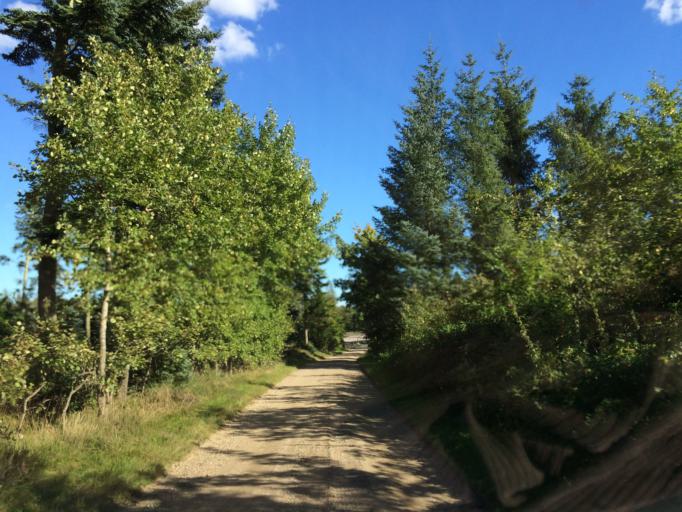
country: DK
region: Central Jutland
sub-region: Holstebro Kommune
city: Ulfborg
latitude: 56.2655
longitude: 8.4293
